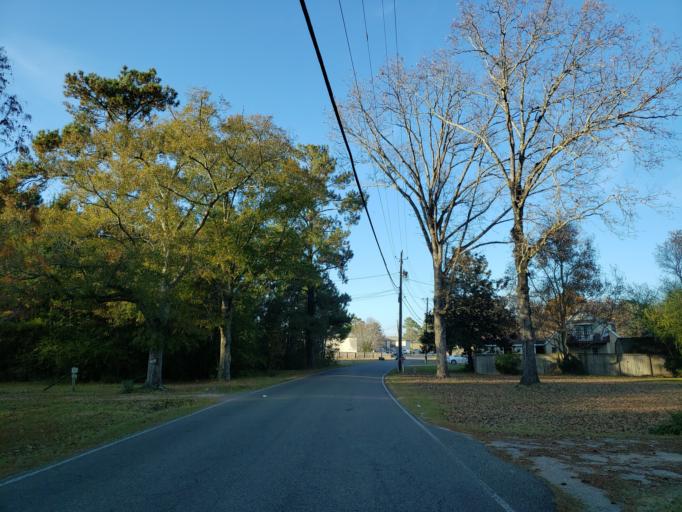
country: US
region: Mississippi
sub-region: Lamar County
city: Arnold Line
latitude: 31.3443
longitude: -89.3604
